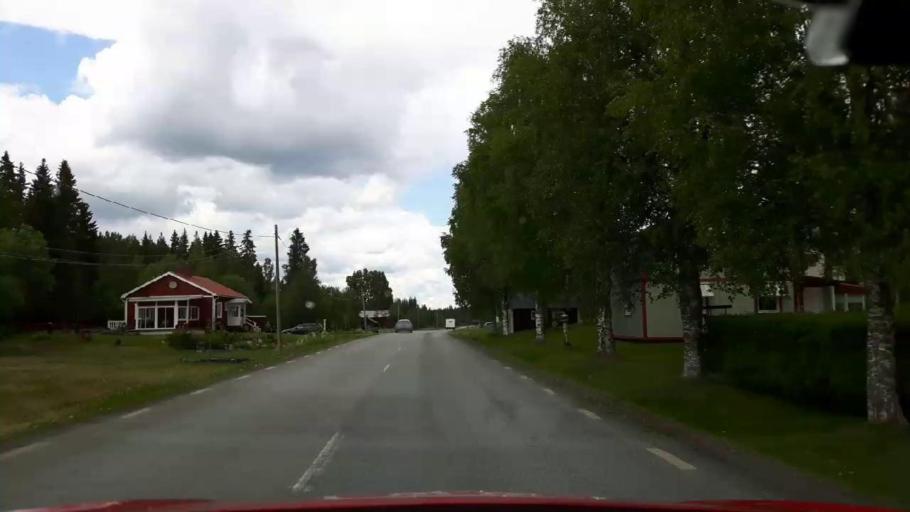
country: SE
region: Jaemtland
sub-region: Krokoms Kommun
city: Krokom
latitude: 63.5180
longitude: 14.2317
